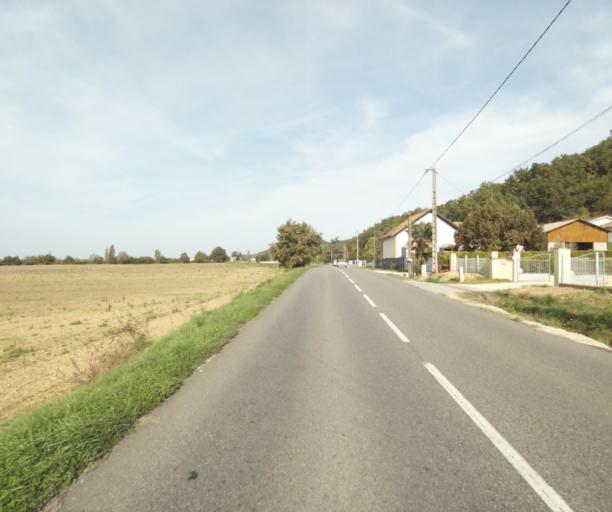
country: FR
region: Midi-Pyrenees
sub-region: Departement du Tarn-et-Garonne
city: Corbarieu
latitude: 43.9516
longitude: 1.3648
